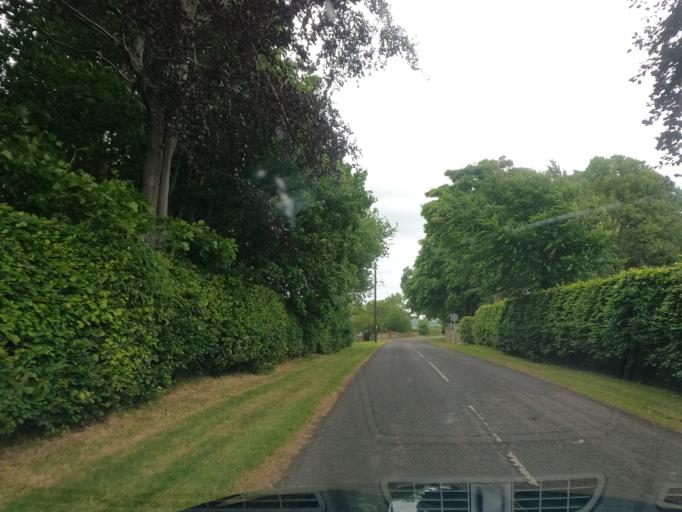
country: GB
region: England
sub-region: Northumberland
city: Doddington
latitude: 55.5595
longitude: -1.9371
